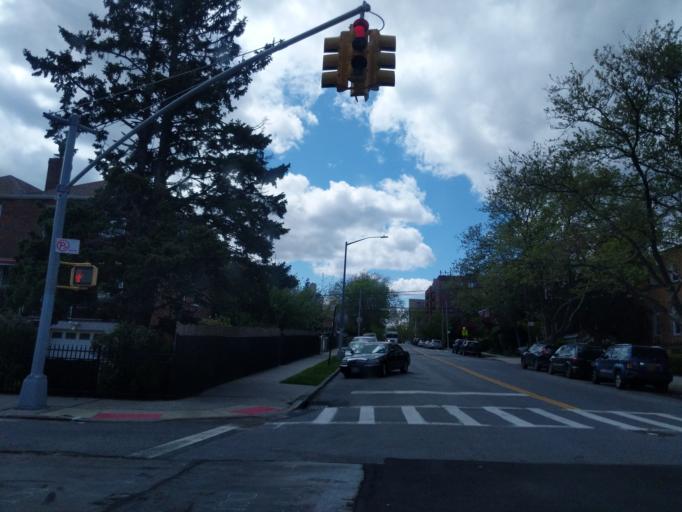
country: US
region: New York
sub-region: Bronx
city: The Bronx
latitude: 40.8612
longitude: -73.8618
